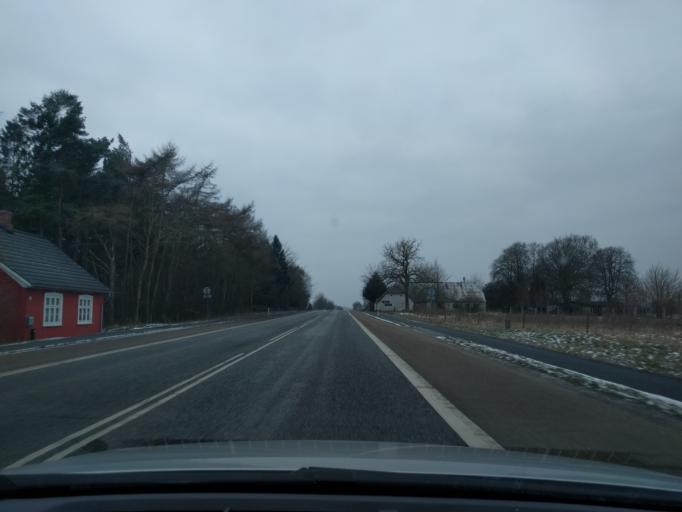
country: DK
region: South Denmark
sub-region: Middelfart Kommune
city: Strib
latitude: 55.4932
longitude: 9.7857
